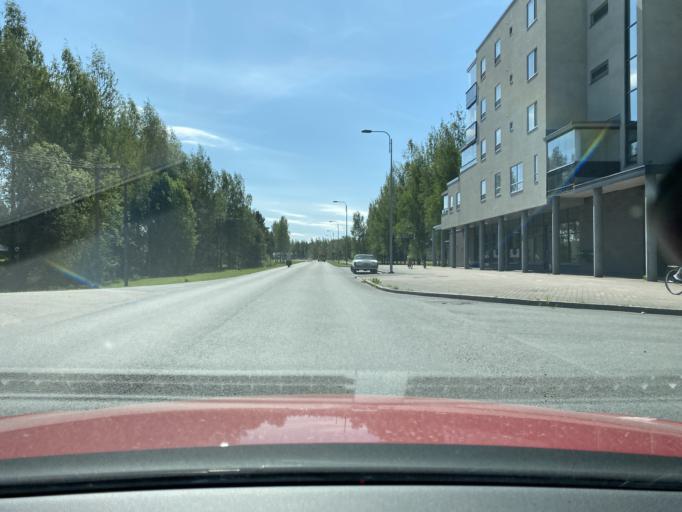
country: FI
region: Satakunta
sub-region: Rauma
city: Eura
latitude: 61.1290
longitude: 22.1444
